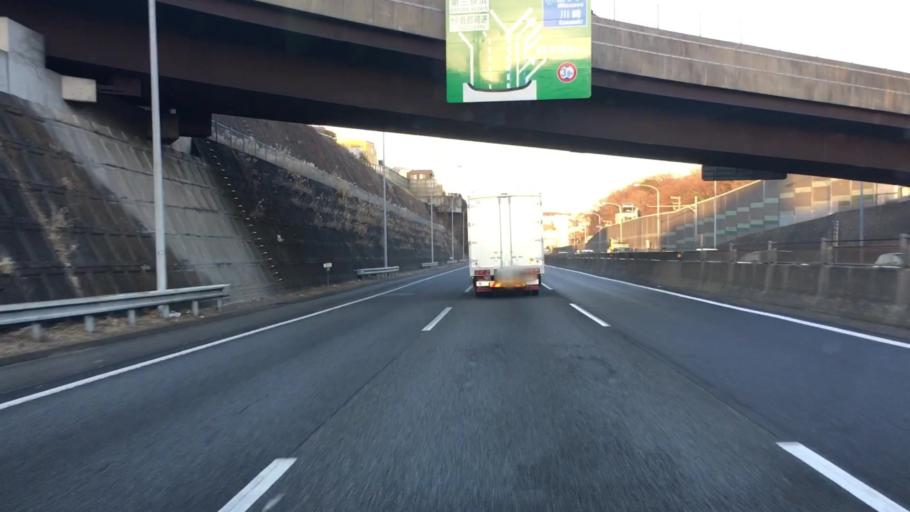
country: JP
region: Kanagawa
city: Yokohama
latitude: 35.4563
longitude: 139.5825
